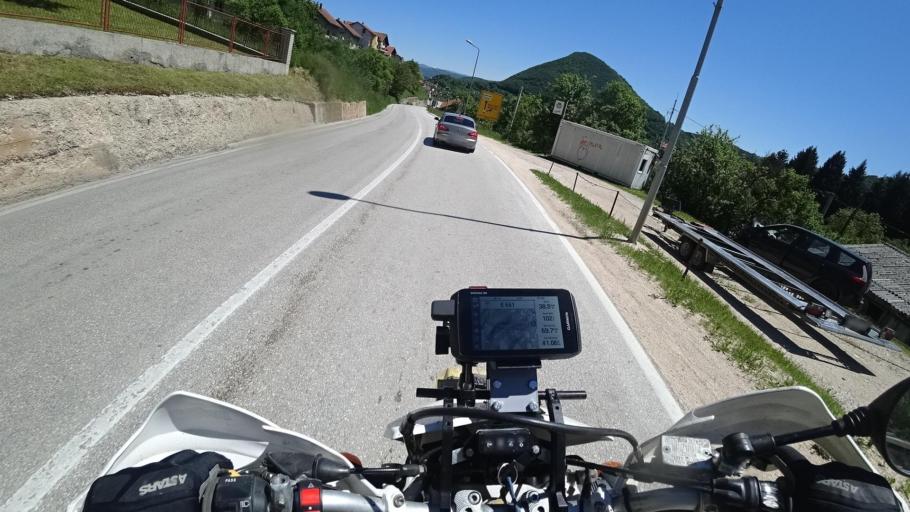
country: BA
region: Republika Srpska
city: Mrkonjic Grad
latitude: 44.4126
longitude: 17.0772
